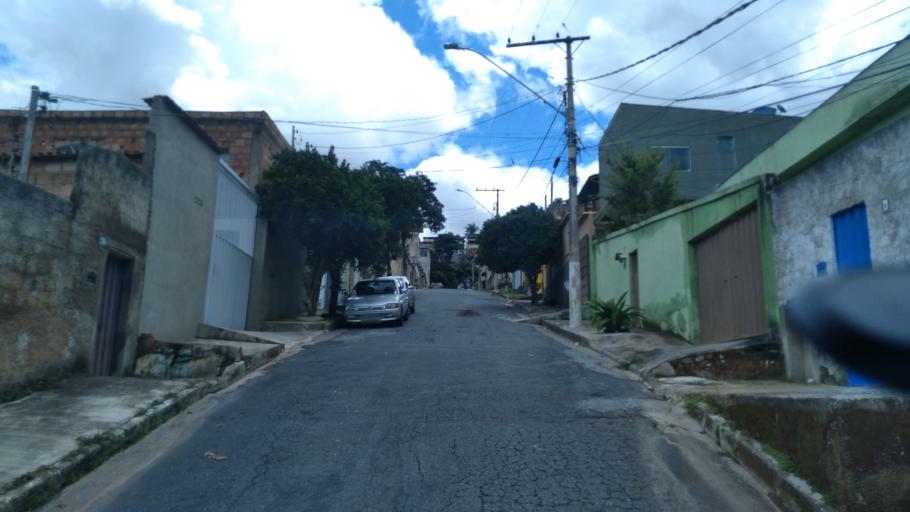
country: BR
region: Minas Gerais
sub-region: Belo Horizonte
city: Belo Horizonte
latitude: -19.8978
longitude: -43.8858
